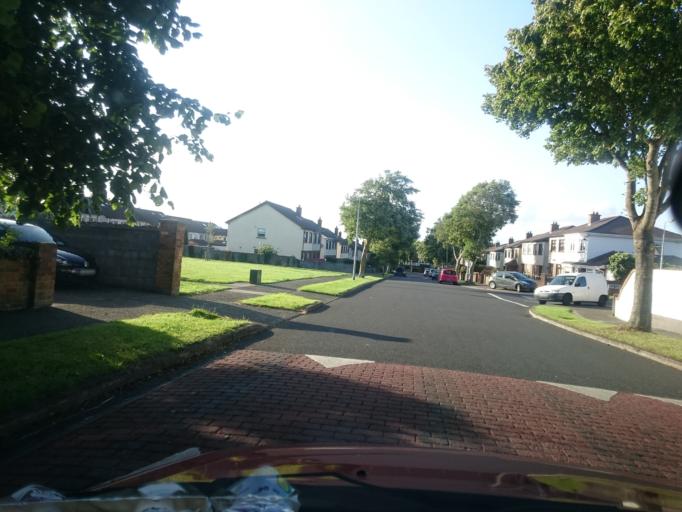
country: IE
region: Leinster
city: Clondalkin
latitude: 53.3125
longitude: -6.4007
